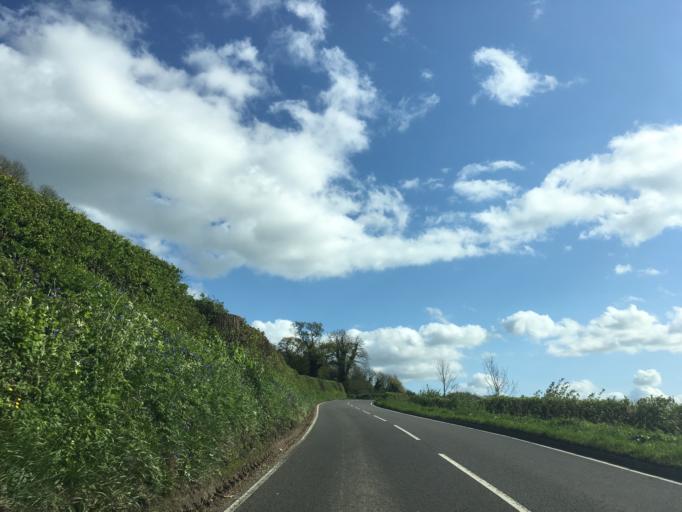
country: GB
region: England
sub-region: Gloucestershire
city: Stonehouse
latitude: 51.7116
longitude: -2.3027
